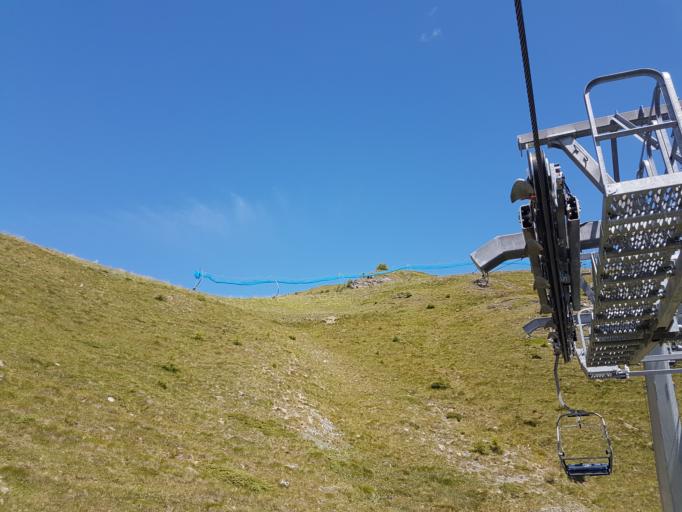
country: IT
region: Aosta Valley
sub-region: Valle d'Aosta
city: Chamois
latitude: 45.8506
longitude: 7.6396
